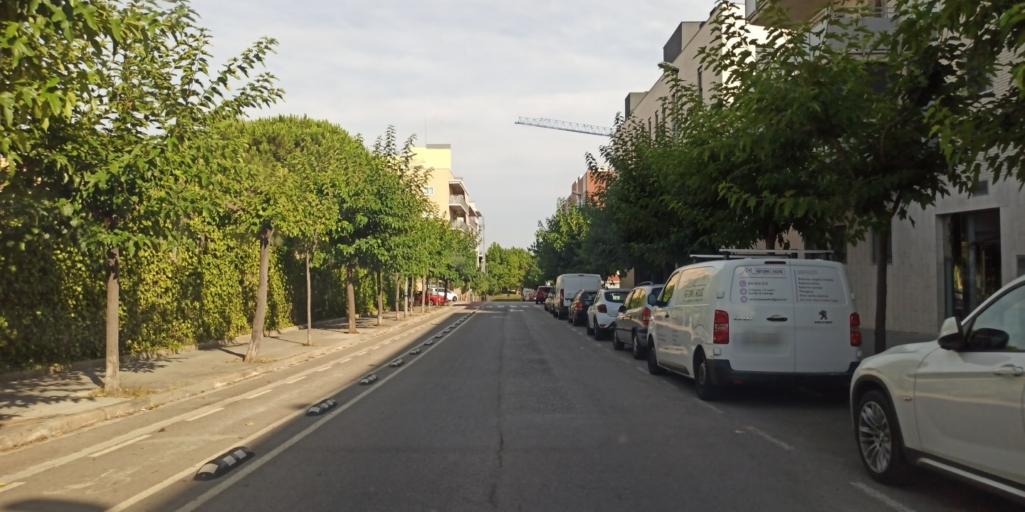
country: ES
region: Catalonia
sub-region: Provincia de Barcelona
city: Santa Coloma de Cervello
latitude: 41.3550
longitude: 2.0249
